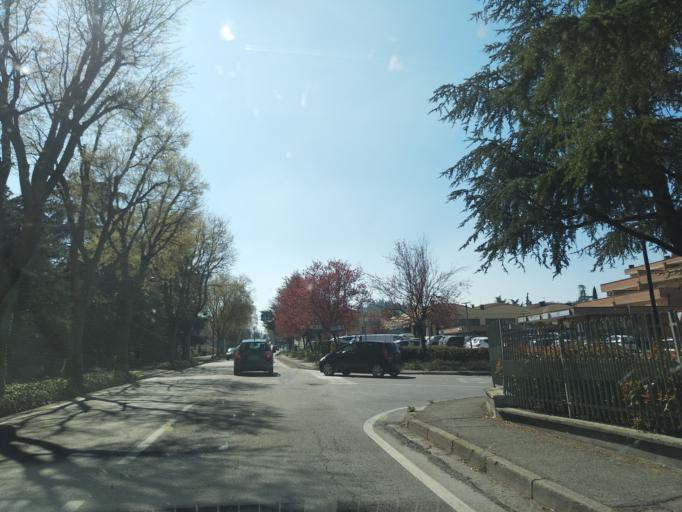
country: IT
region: Emilia-Romagna
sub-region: Provincia di Reggio Emilia
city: Albinea
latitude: 44.6227
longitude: 10.6043
